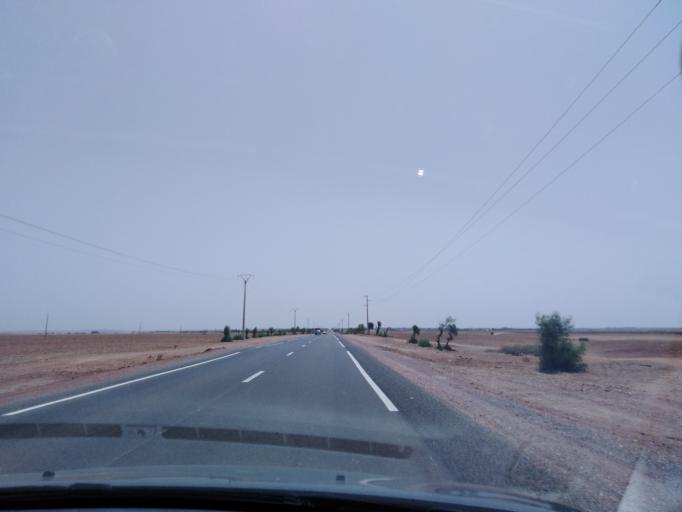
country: MA
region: Doukkala-Abda
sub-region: Safi
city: Youssoufia
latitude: 32.0993
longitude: -8.6709
